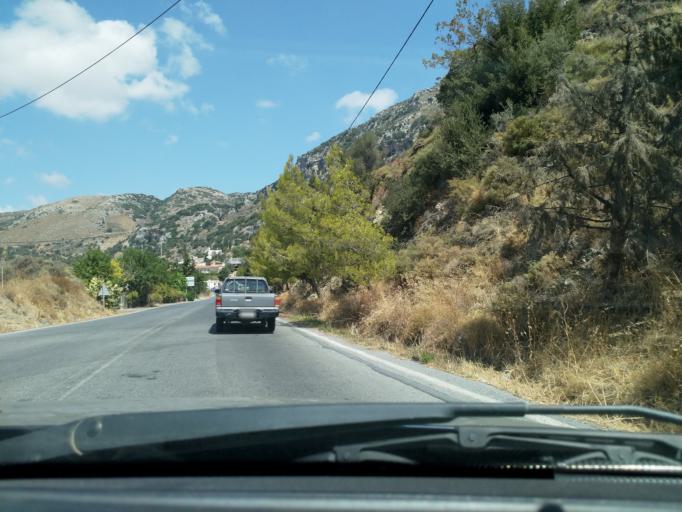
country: GR
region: Crete
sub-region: Nomos Rethymnis
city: Agia Foteini
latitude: 35.2099
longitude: 24.5345
